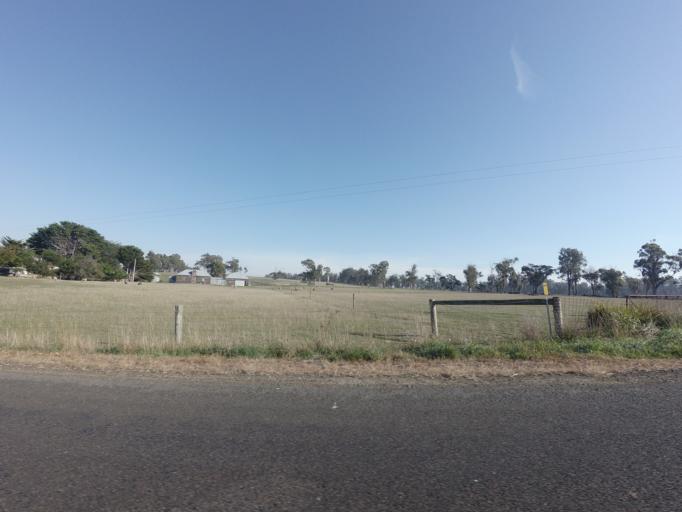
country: AU
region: Tasmania
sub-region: Northern Midlands
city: Longford
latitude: -41.5408
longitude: 146.9920
